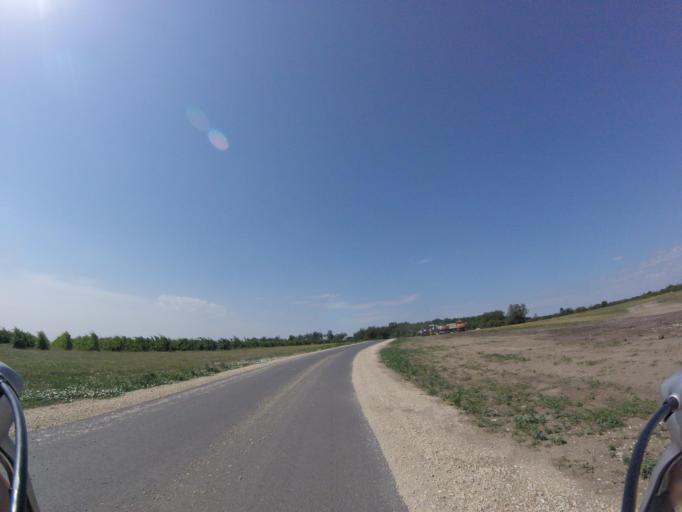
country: HU
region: Fejer
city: Etyek
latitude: 47.4251
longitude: 18.7282
